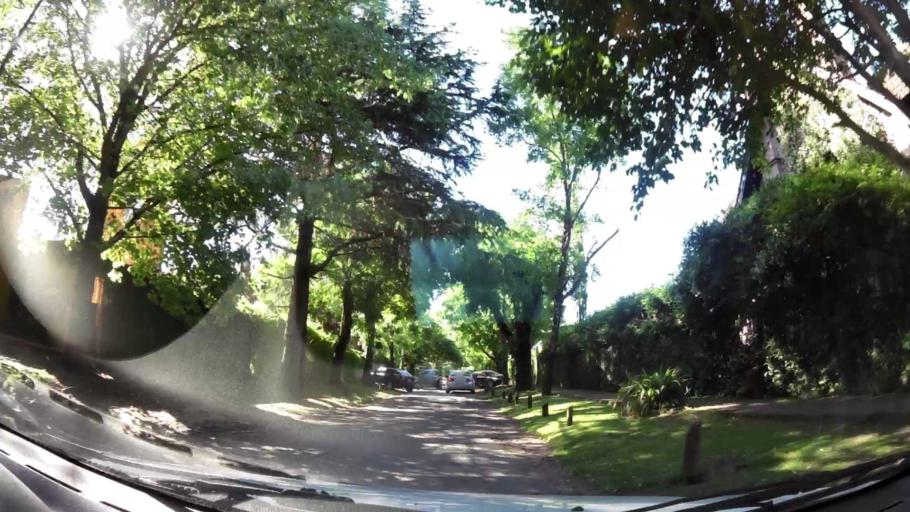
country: AR
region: Buenos Aires
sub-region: Partido de San Isidro
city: San Isidro
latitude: -34.4824
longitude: -58.5423
